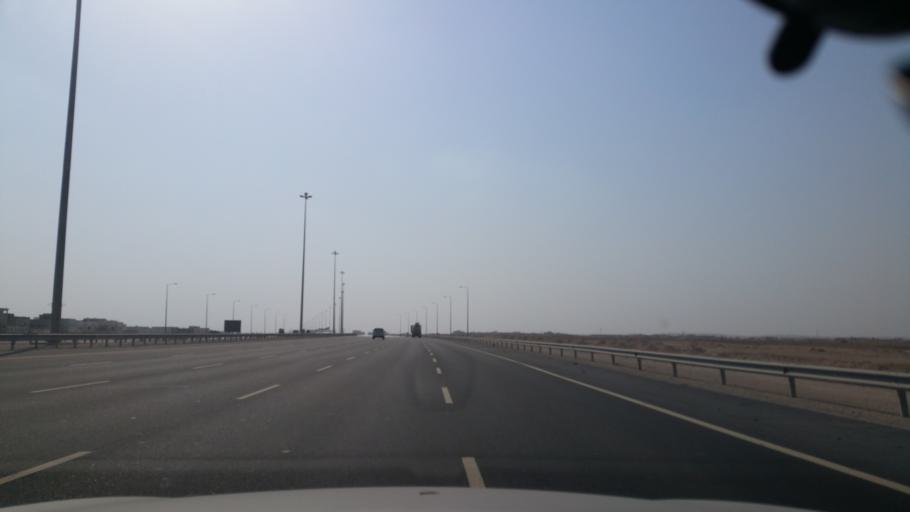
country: QA
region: Baladiyat Umm Salal
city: Umm Salal `Ali
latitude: 25.4570
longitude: 51.4441
